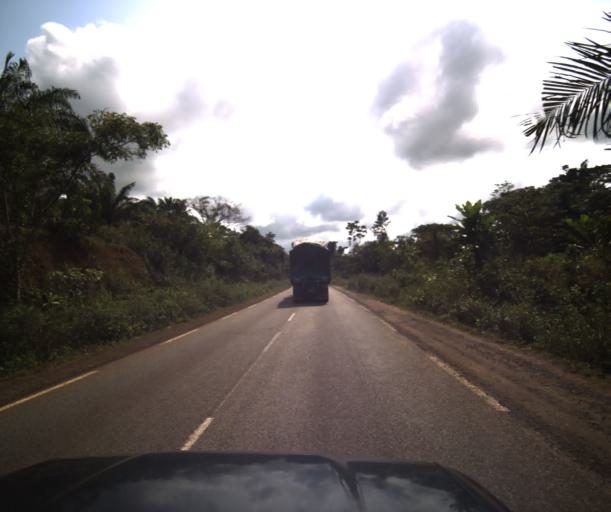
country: CM
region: Littoral
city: Edea
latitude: 3.8027
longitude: 10.2425
